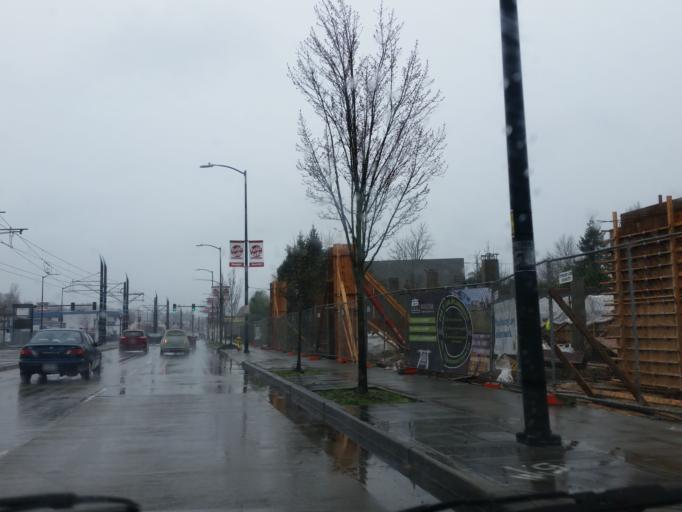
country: US
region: Washington
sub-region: King County
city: Riverton
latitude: 47.5396
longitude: -122.2822
